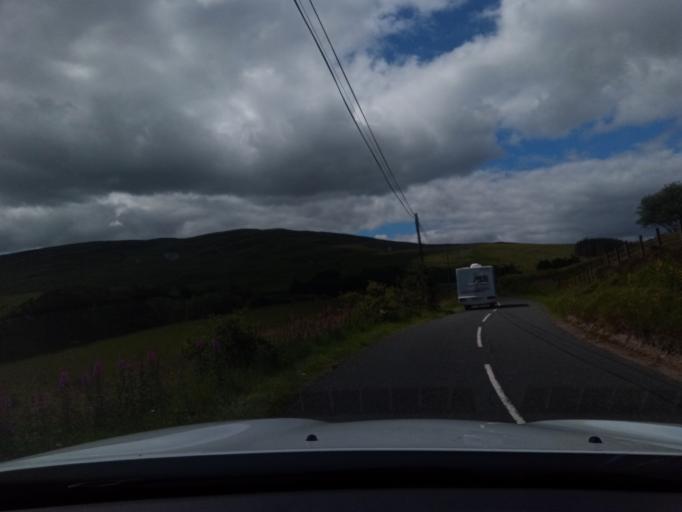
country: GB
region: Scotland
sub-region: The Scottish Borders
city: Innerleithen
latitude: 55.5407
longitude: -3.0024
